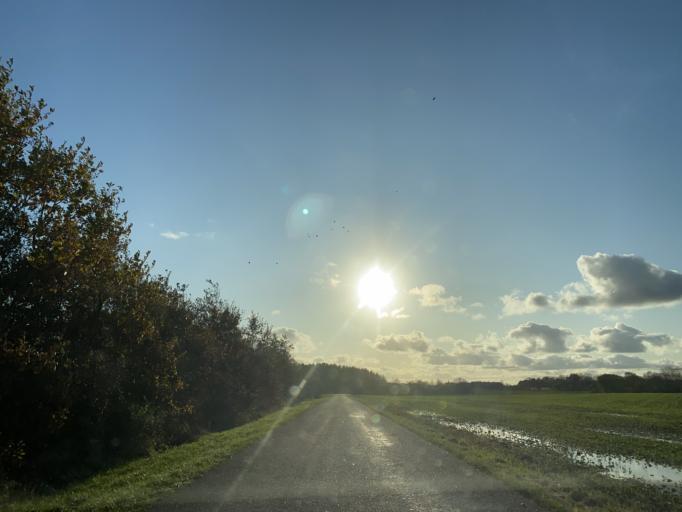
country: DK
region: Central Jutland
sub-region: Viborg Kommune
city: Bjerringbro
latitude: 56.3265
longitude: 9.7067
